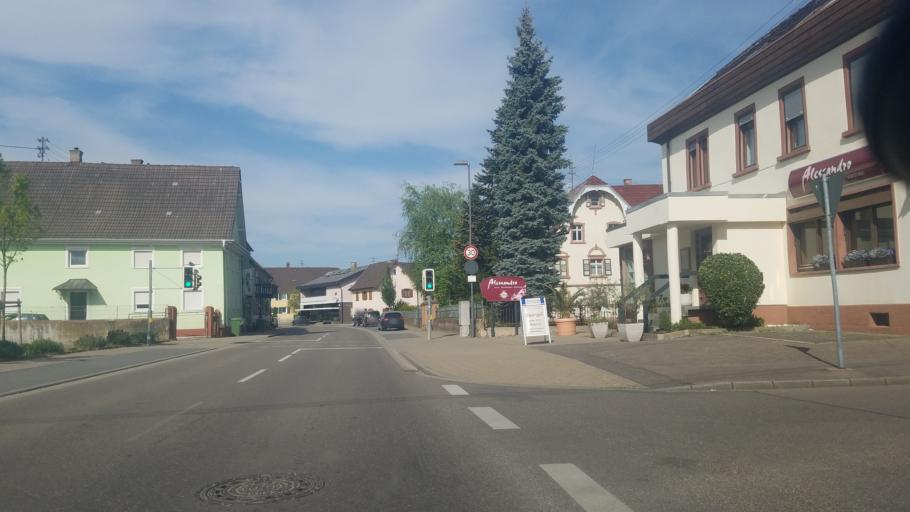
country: DE
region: Baden-Wuerttemberg
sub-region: Freiburg Region
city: Meissenheim
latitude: 48.4641
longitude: 7.8131
